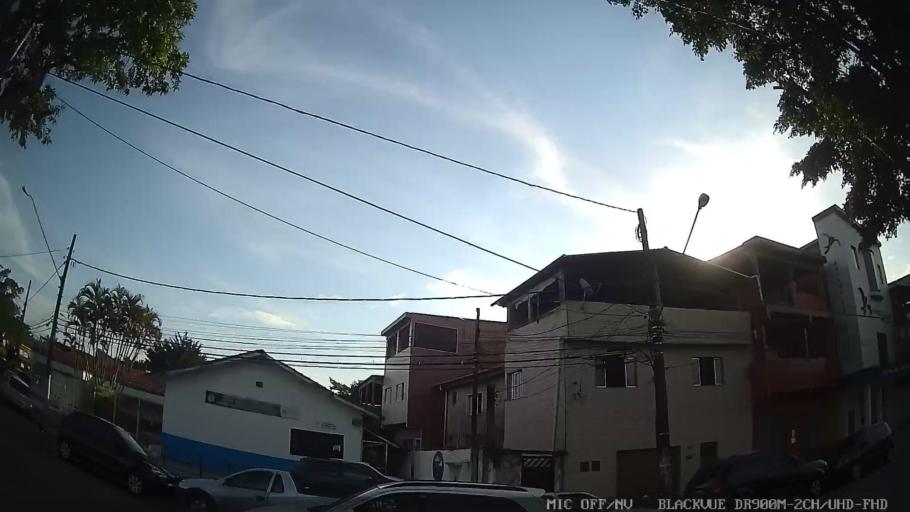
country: BR
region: Sao Paulo
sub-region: Cubatao
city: Cubatao
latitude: -23.9062
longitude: -46.4233
